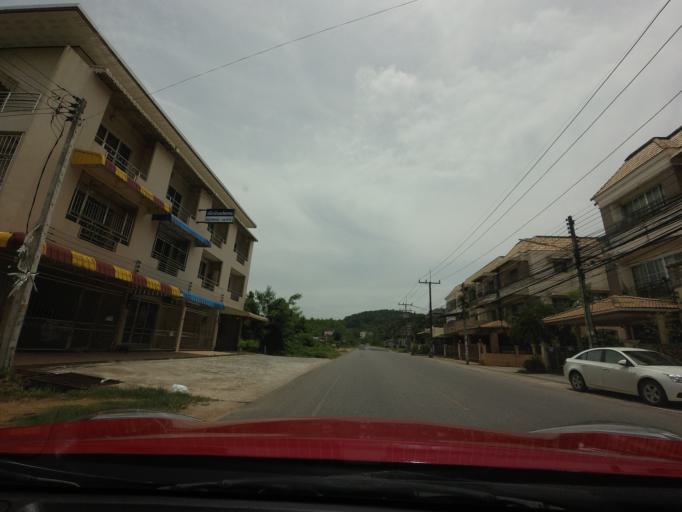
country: TH
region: Songkhla
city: Hat Yai
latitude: 7.0001
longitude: 100.5193
